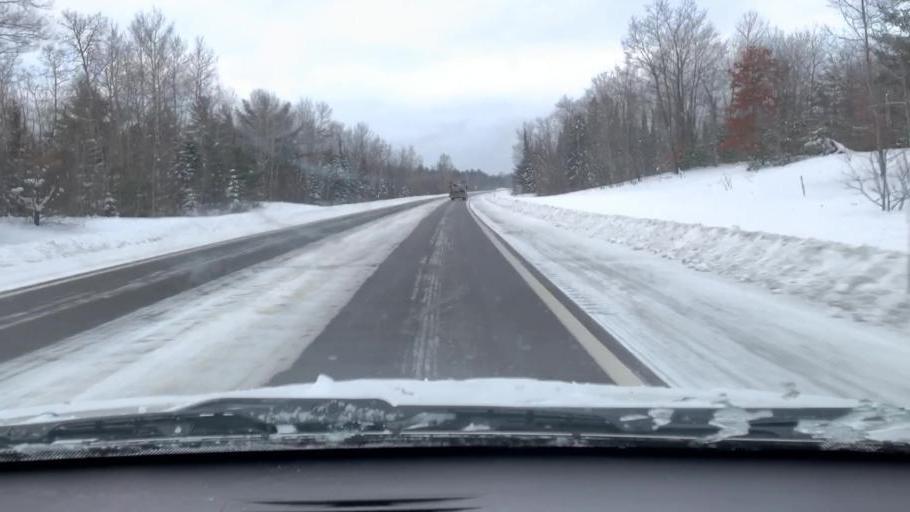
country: US
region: Michigan
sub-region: Kalkaska County
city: Kalkaska
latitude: 44.6547
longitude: -85.2612
